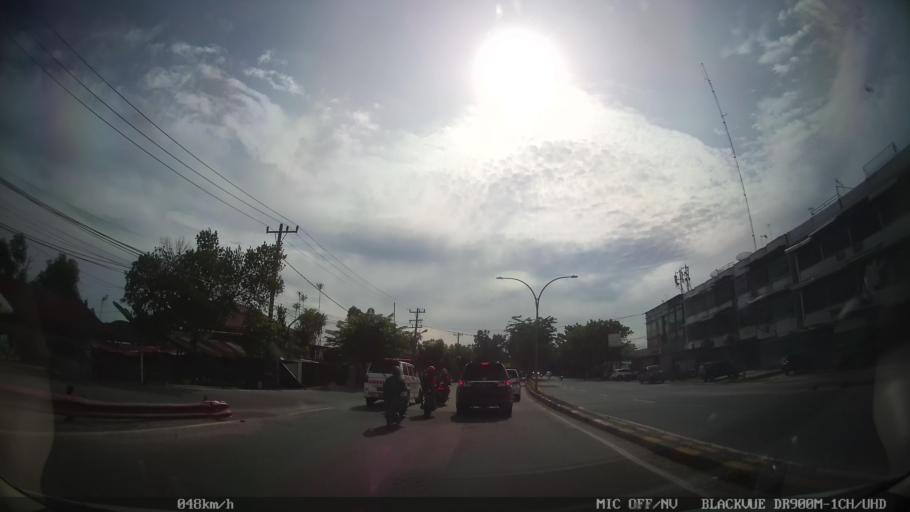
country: ID
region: North Sumatra
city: Medan
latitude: 3.6302
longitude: 98.6737
